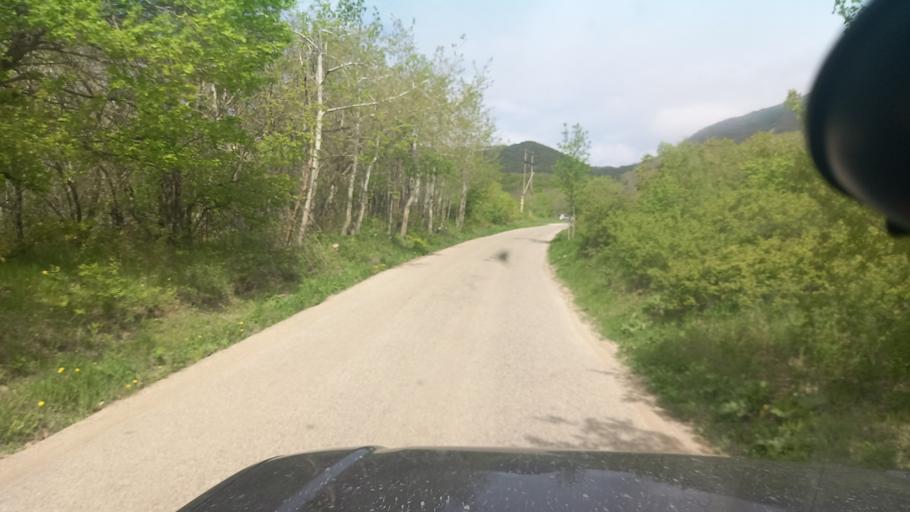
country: RU
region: Stavropol'skiy
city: Pyatigorsk
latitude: 44.0833
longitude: 43.0333
